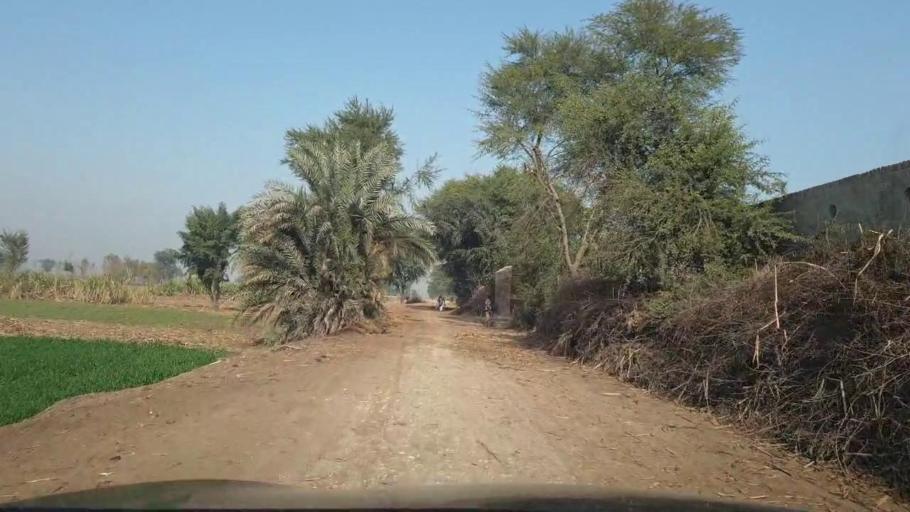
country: PK
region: Sindh
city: Ubauro
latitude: 28.1209
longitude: 69.7509
